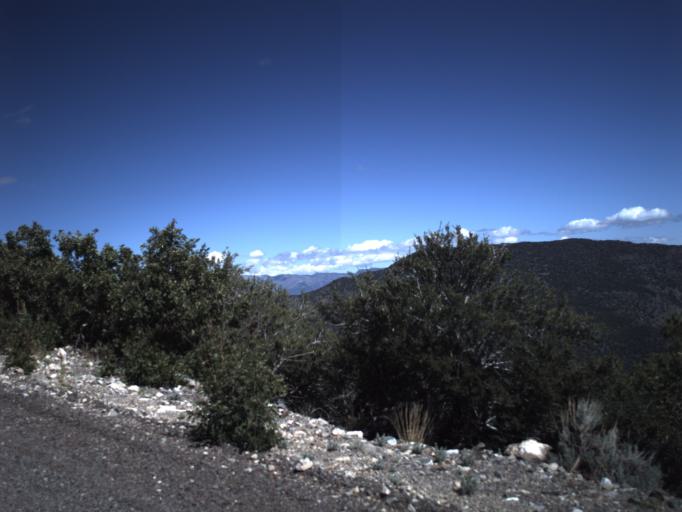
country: US
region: Utah
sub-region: Piute County
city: Junction
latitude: 38.2558
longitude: -112.3157
